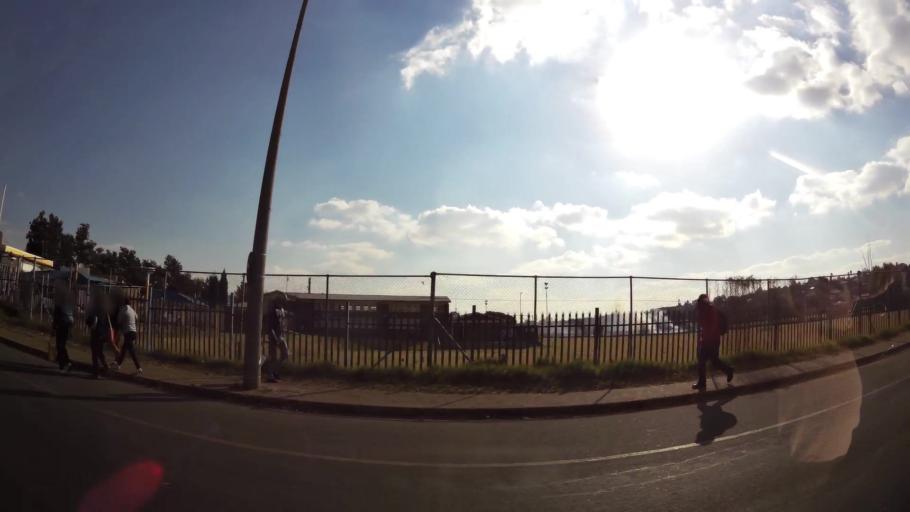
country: ZA
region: Gauteng
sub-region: West Rand District Municipality
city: Krugersdorp
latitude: -26.0975
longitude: 27.7749
